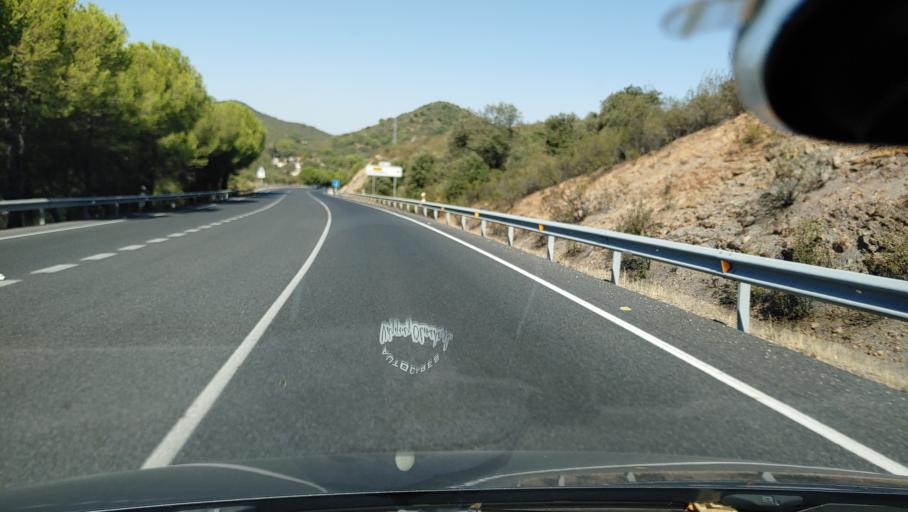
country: ES
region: Andalusia
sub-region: Province of Cordoba
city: Villaharta
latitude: 38.1200
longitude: -4.8913
